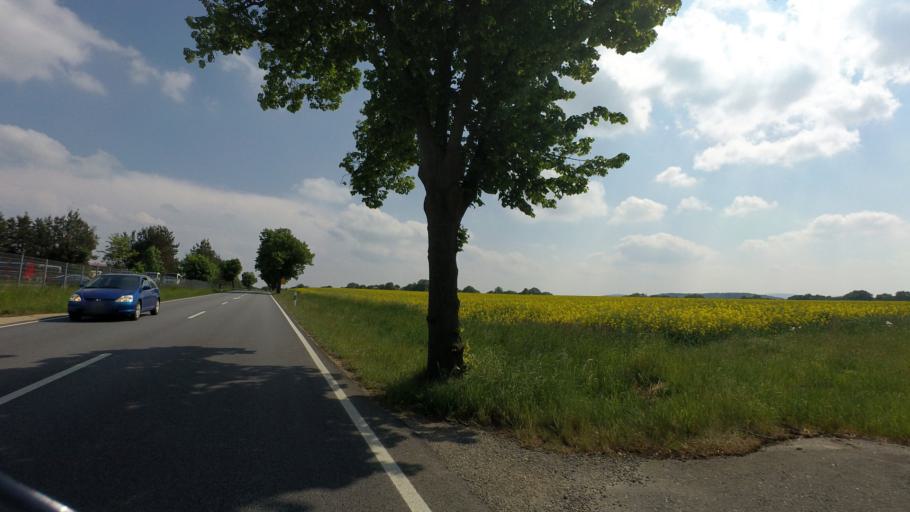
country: DE
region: Saxony
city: Weissenberg
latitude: 51.1961
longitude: 14.6701
